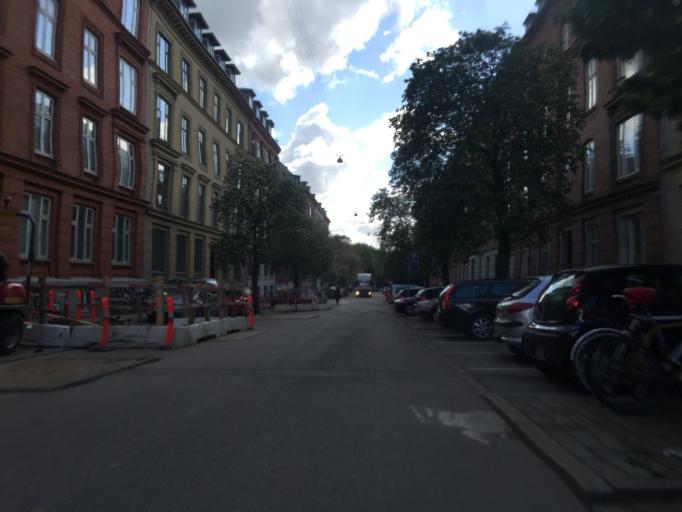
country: DK
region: Capital Region
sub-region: Frederiksberg Kommune
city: Frederiksberg
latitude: 55.6762
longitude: 12.5355
